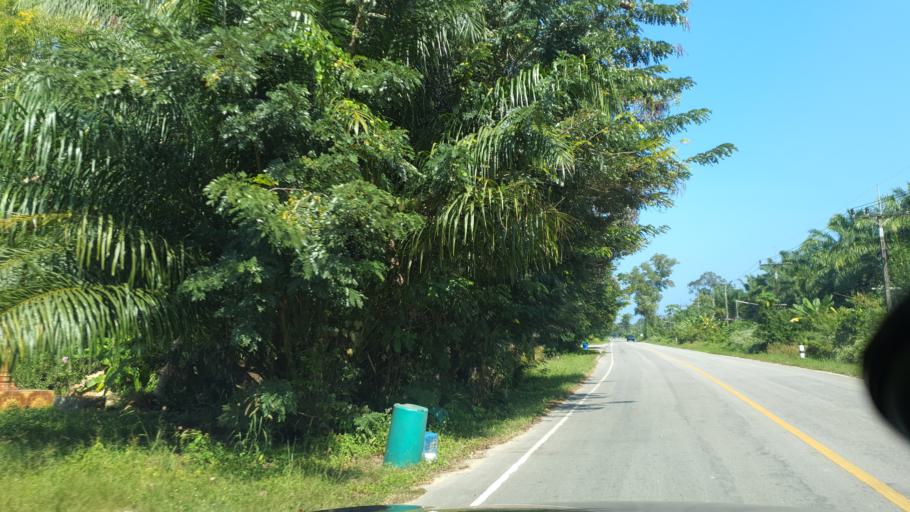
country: TH
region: Surat Thani
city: Tha Chana
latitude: 9.5775
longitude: 99.1865
